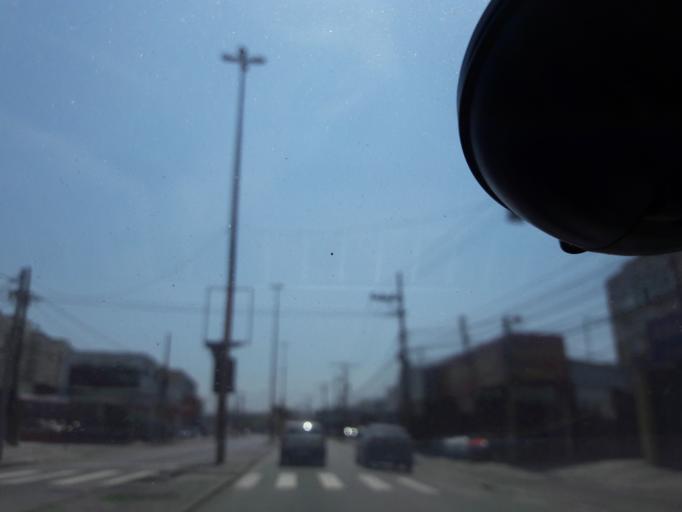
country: BR
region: Rio de Janeiro
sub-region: Sao Joao De Meriti
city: Sao Joao de Meriti
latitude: -22.8788
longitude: -43.3576
